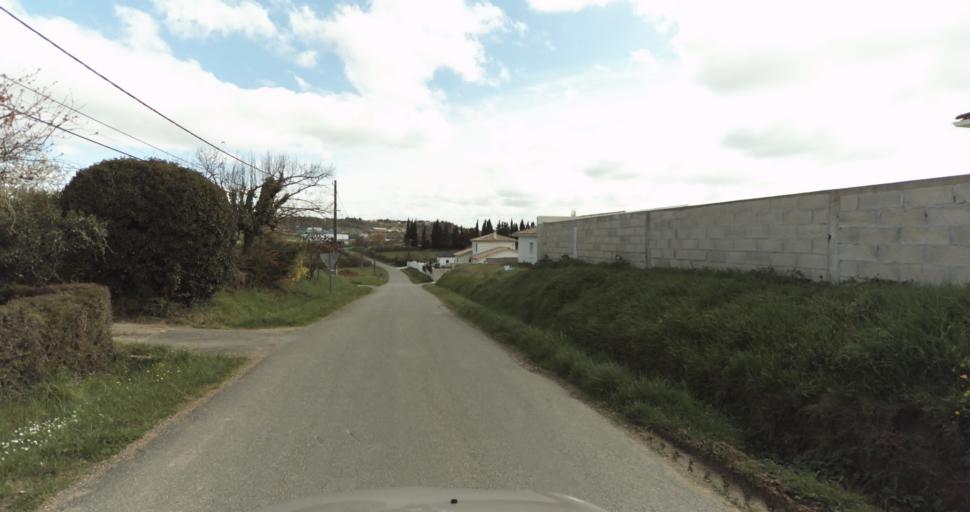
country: FR
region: Midi-Pyrenees
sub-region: Departement du Tarn
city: Puygouzon
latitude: 43.8887
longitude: 2.1542
